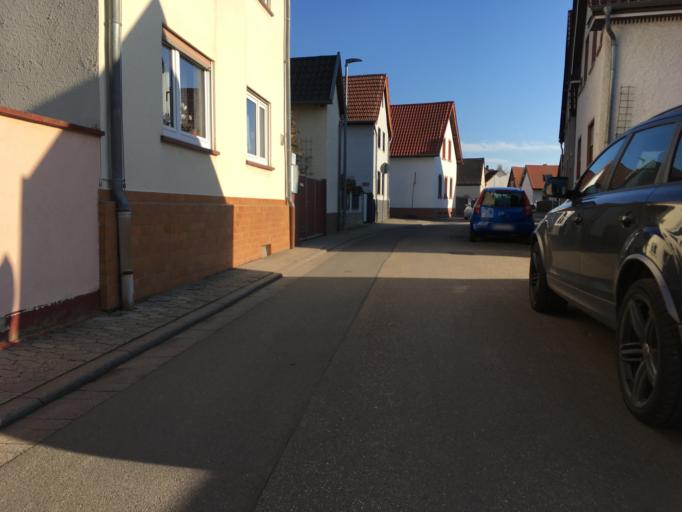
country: DE
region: Rheinland-Pfalz
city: Worms
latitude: 49.6826
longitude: 8.3856
